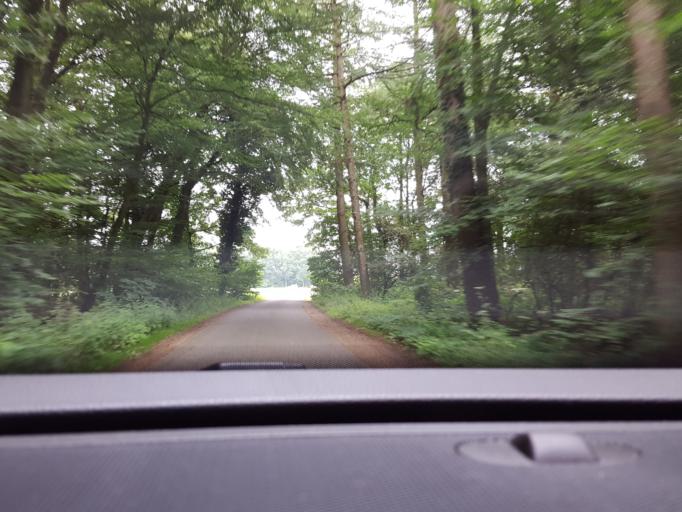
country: NL
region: Gelderland
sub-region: Gemeente Zutphen
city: Leesten
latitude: 52.1165
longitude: 6.2692
